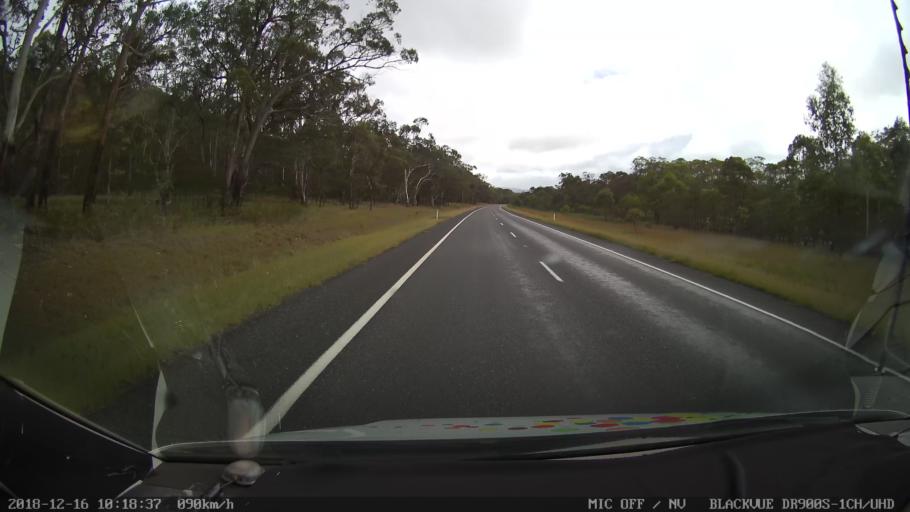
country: AU
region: New South Wales
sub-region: Tenterfield Municipality
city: Carrolls Creek
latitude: -29.2412
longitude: 151.9990
